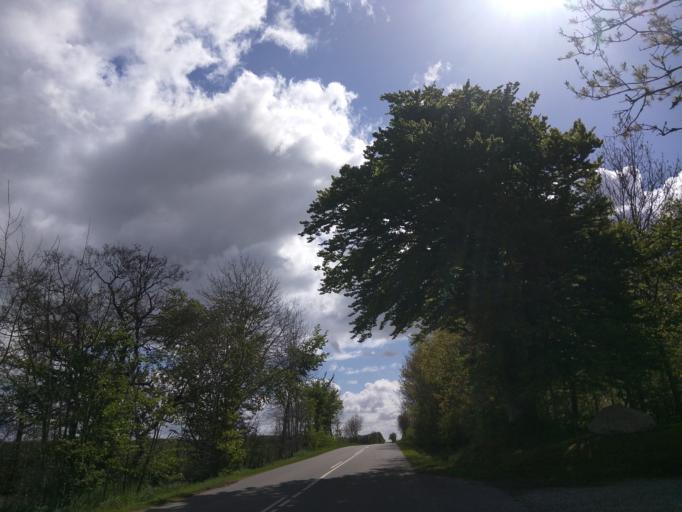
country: DK
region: Central Jutland
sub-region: Silkeborg Kommune
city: Kjellerup
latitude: 56.2866
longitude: 9.4512
